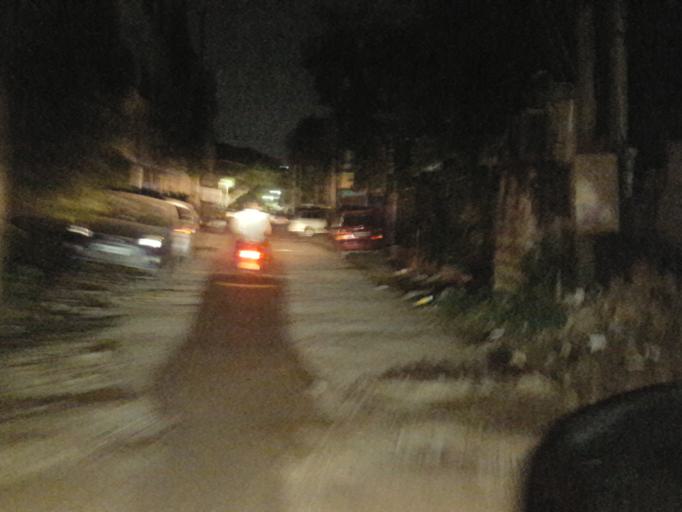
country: IN
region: Telangana
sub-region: Rangareddi
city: Kukatpalli
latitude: 17.4874
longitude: 78.3938
